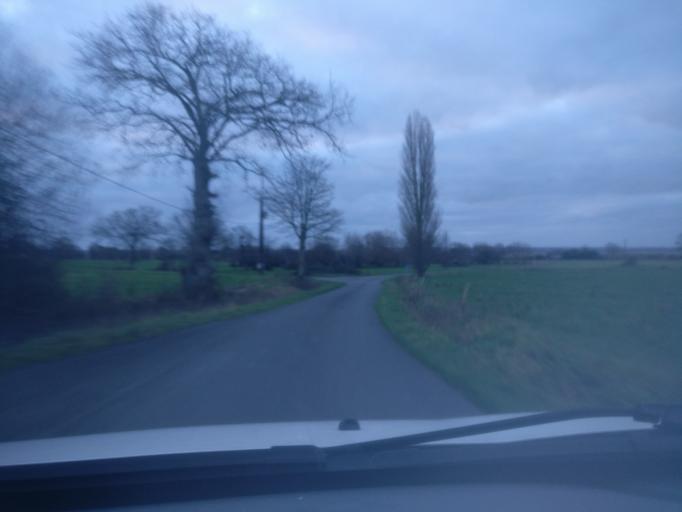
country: FR
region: Lower Normandy
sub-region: Departement de la Manche
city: Marcey-les-Greves
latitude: 48.6709
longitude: -1.4328
